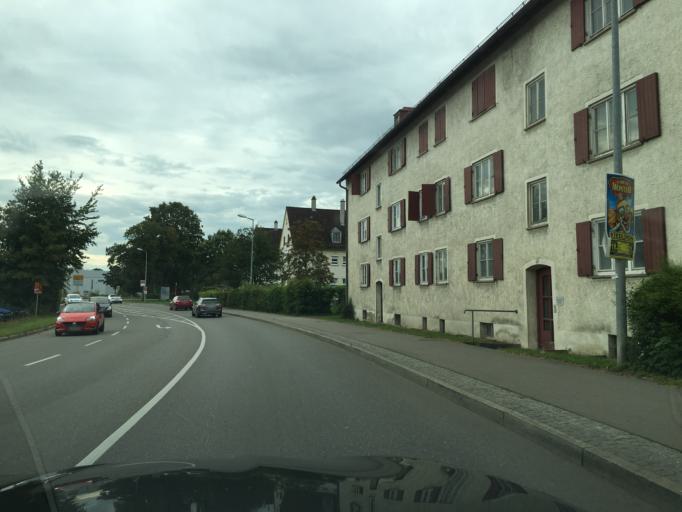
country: DE
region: Baden-Wuerttemberg
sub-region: Tuebingen Region
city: Riedlingen
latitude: 48.1587
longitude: 9.4767
